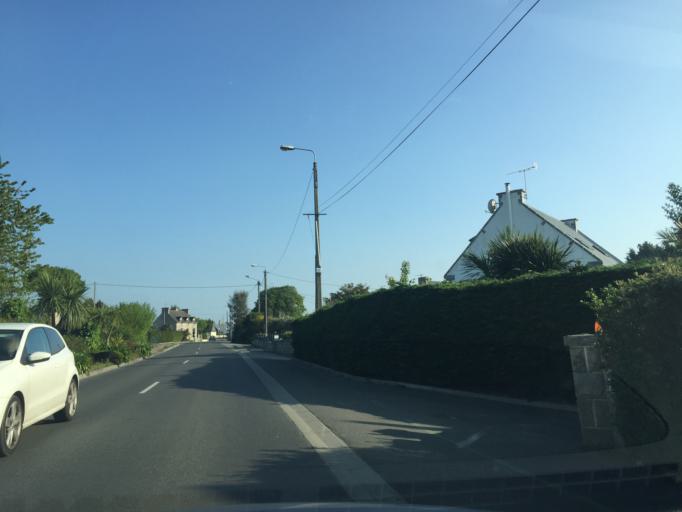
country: FR
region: Brittany
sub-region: Departement des Cotes-d'Armor
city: Saint-Cast-le-Guildo
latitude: 48.6220
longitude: -2.2651
